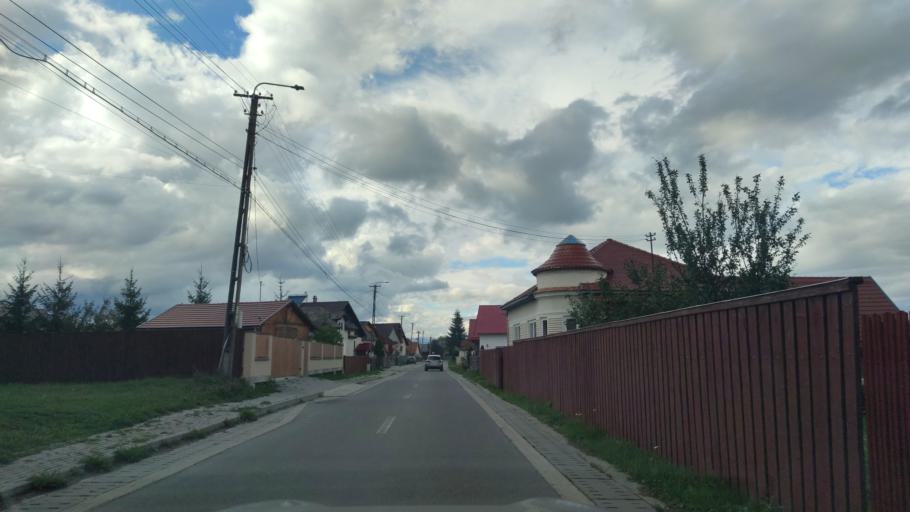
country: RO
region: Harghita
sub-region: Comuna Remetea
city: Remetea
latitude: 46.8027
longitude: 25.4502
